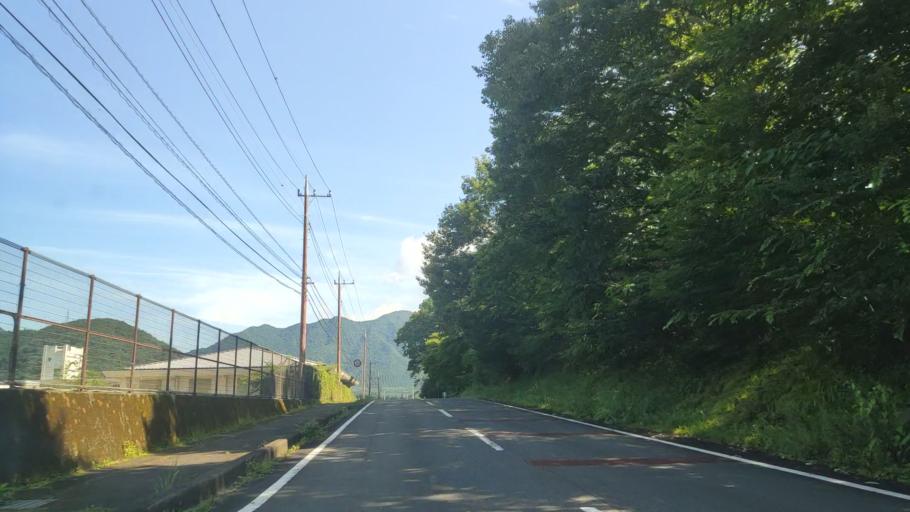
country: JP
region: Tochigi
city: Imaichi
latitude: 36.8407
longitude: 139.7250
